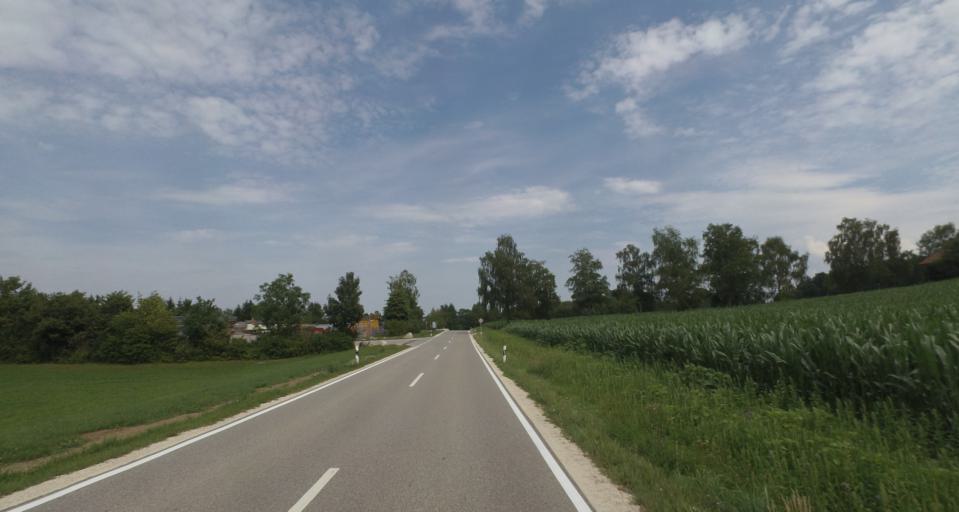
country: DE
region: Bavaria
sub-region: Upper Bavaria
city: Traunreut
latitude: 47.9560
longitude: 12.5599
